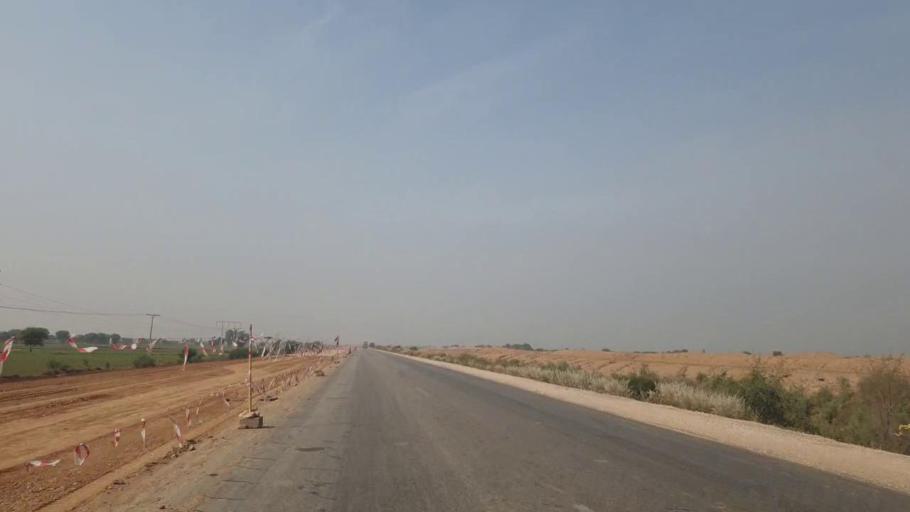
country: PK
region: Sindh
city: Sann
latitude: 26.1367
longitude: 68.0430
